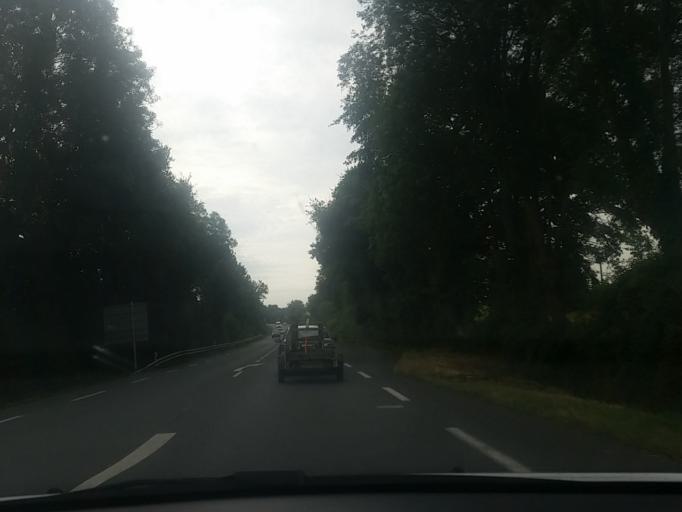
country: FR
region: Pays de la Loire
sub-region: Departement de la Vendee
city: Chavagnes-en-Paillers
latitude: 46.8958
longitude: -1.2264
